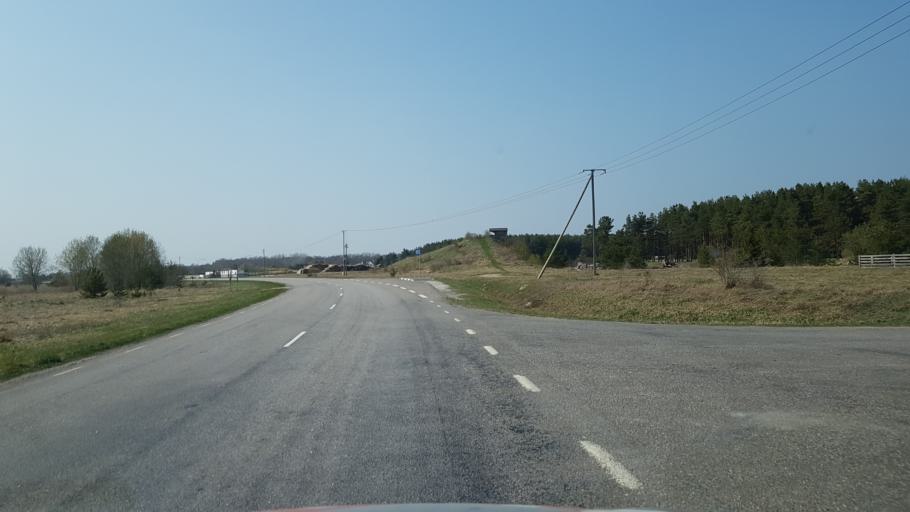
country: EE
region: Harju
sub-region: Paldiski linn
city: Paldiski
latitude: 59.3265
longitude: 24.1191
